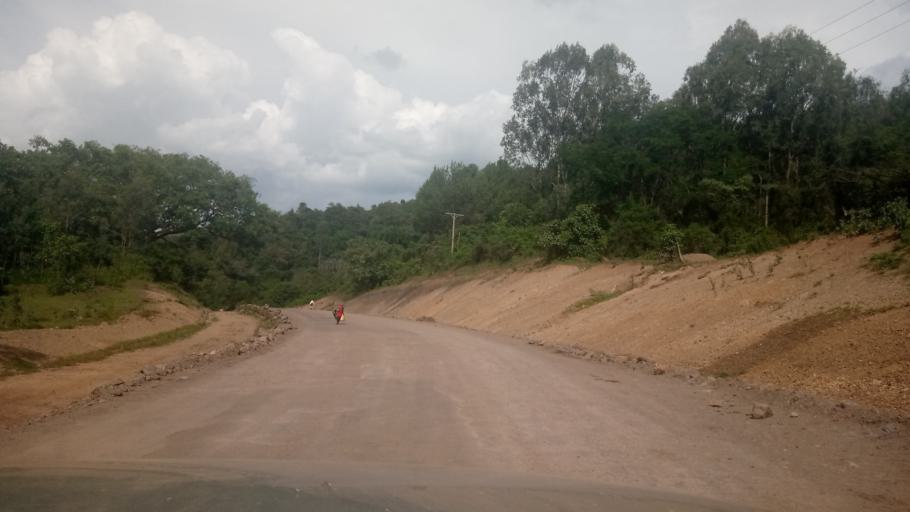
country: ET
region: Oromiya
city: Agaro
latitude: 8.0424
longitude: 36.4681
